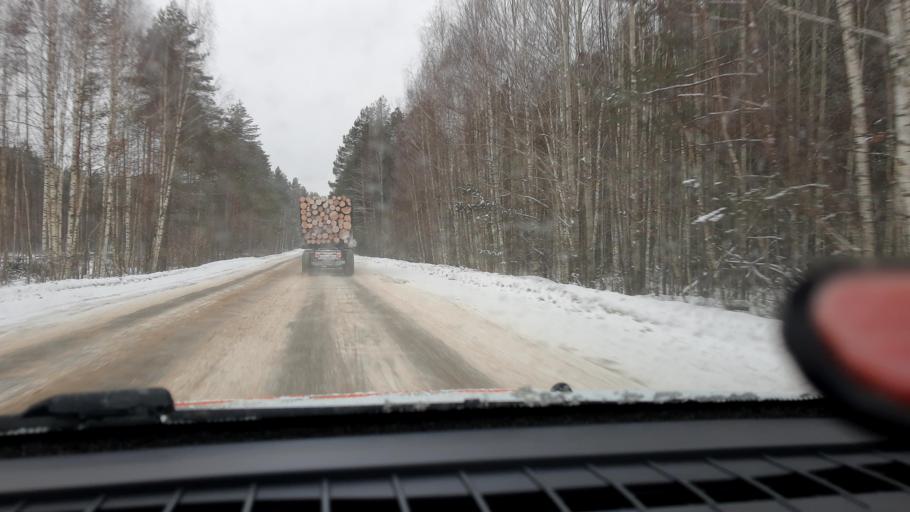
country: RU
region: Nizjnij Novgorod
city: Pamyat' Parizhskoy Kommuny
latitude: 56.2769
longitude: 44.3929
